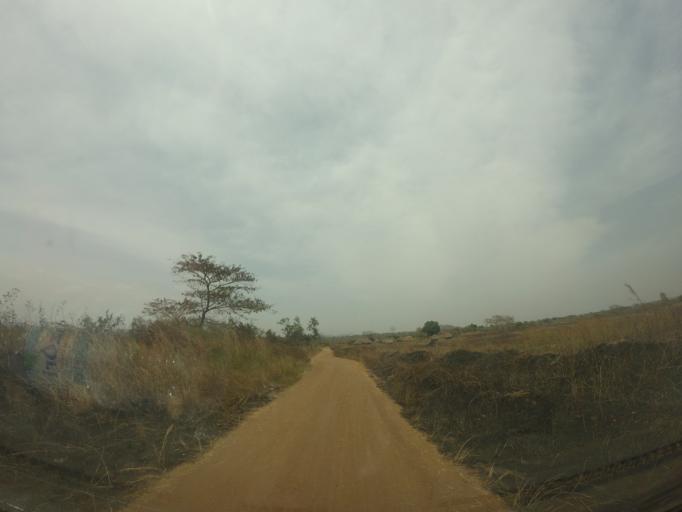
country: UG
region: Northern Region
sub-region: Nebbi District
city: Nebbi
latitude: 2.6259
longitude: 31.0388
